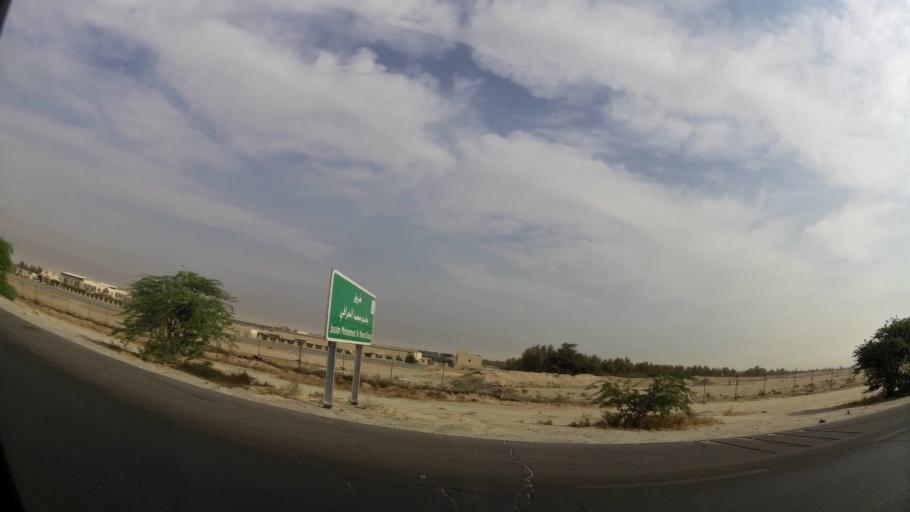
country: KW
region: Al Asimah
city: Ar Rabiyah
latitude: 29.2769
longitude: 47.8044
